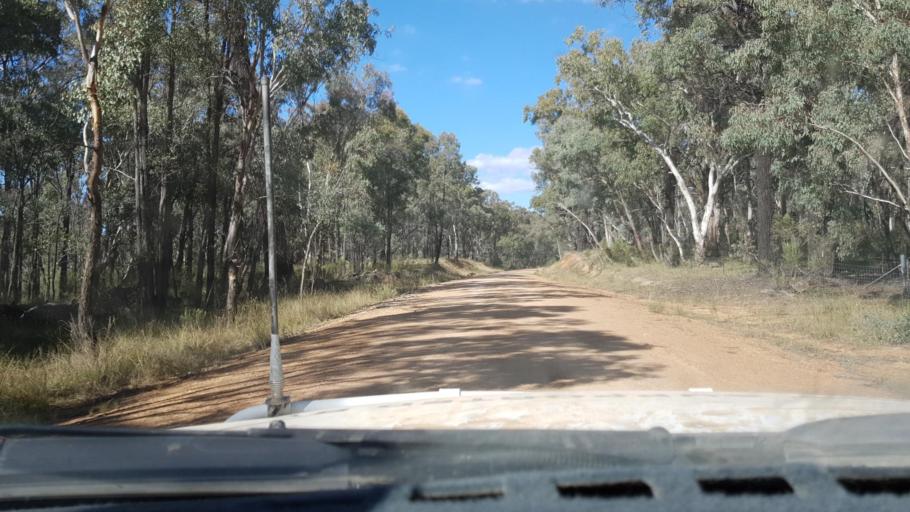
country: AU
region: New South Wales
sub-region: Tamworth Municipality
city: Manilla
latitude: -30.4481
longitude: 150.8745
